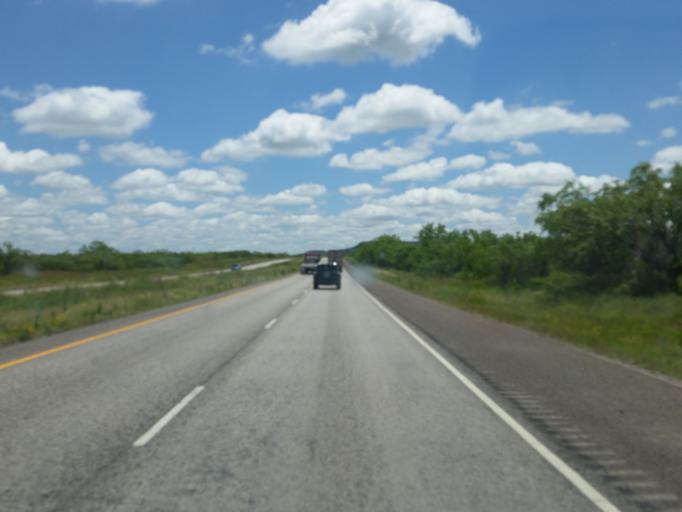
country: US
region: Texas
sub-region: Scurry County
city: Snyder
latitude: 32.9818
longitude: -101.1149
